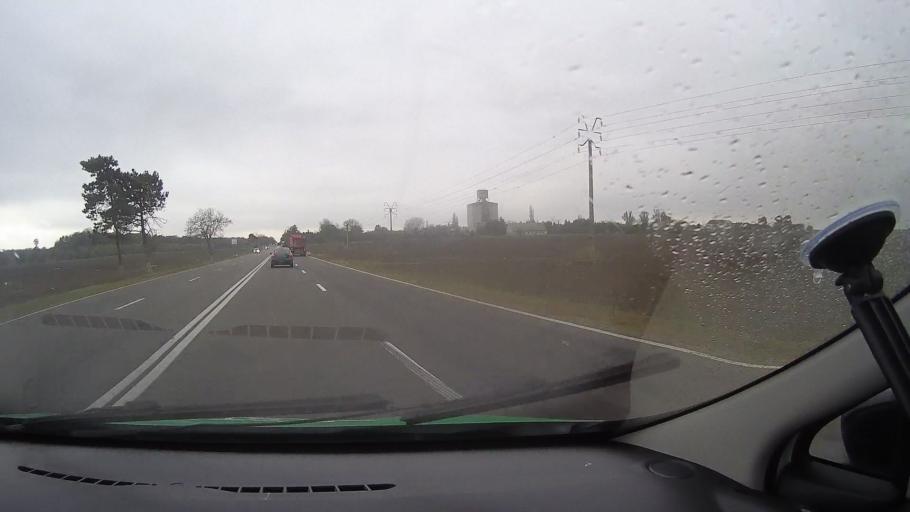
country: RO
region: Constanta
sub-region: Comuna Valu lui Traian
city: Valu lui Traian
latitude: 44.1655
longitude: 28.5170
